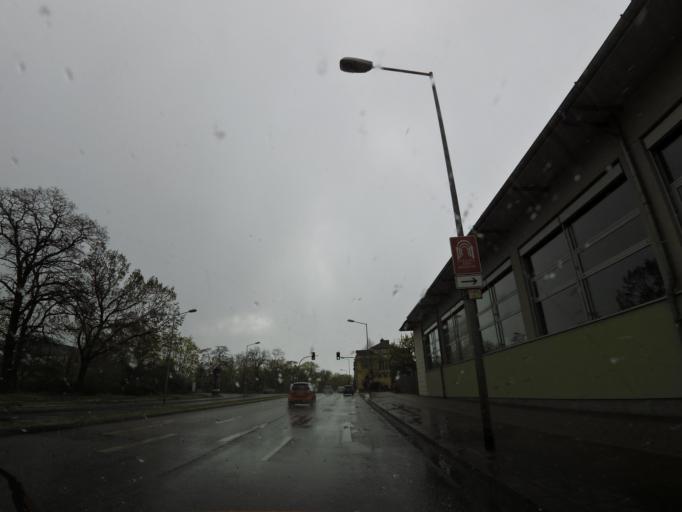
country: DE
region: Saxony-Anhalt
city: Magdeburg
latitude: 52.1171
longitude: 11.6306
